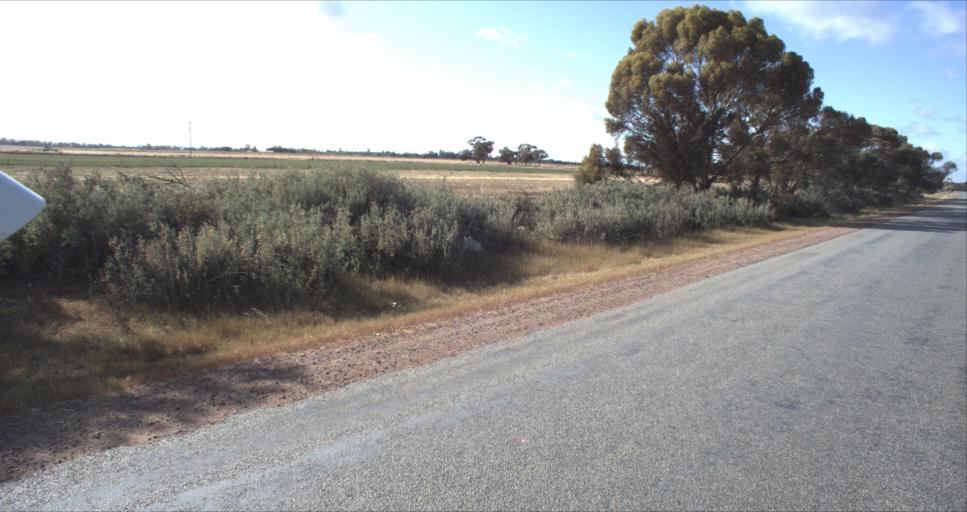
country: AU
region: New South Wales
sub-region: Leeton
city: Leeton
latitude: -34.5077
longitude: 146.3928
